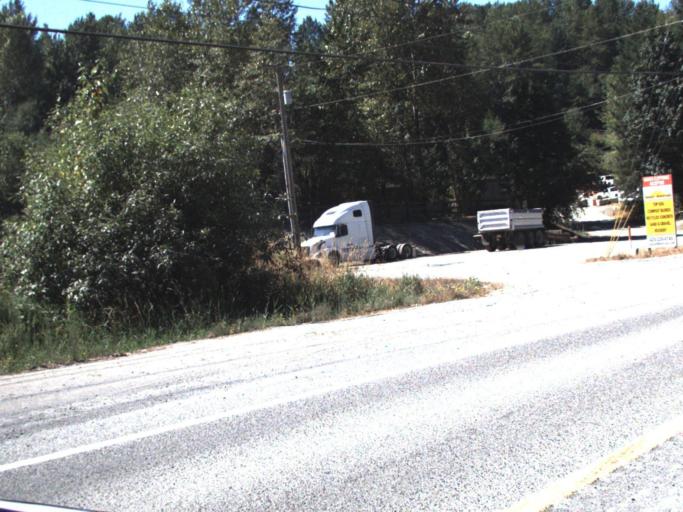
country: US
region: Washington
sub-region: King County
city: East Renton Highlands
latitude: 47.4975
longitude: -122.1009
